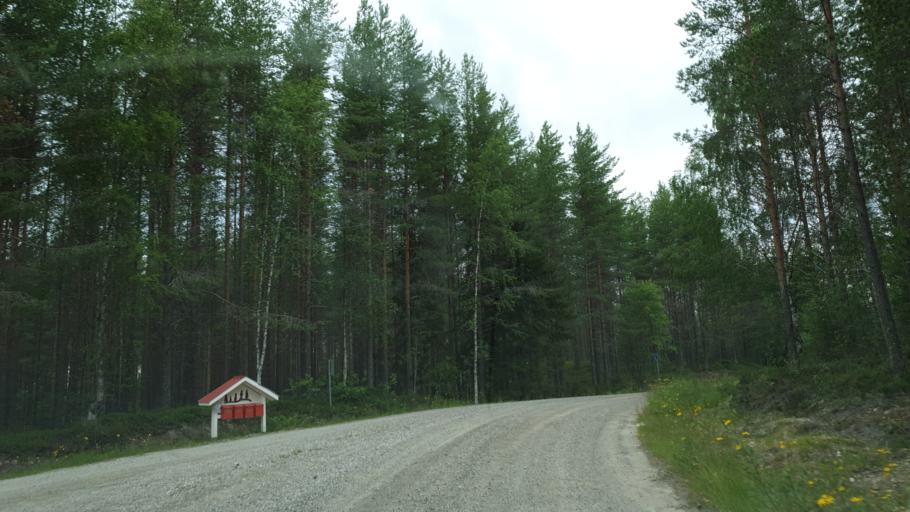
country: FI
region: Kainuu
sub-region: Kehys-Kainuu
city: Kuhmo
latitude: 64.4445
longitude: 29.5564
